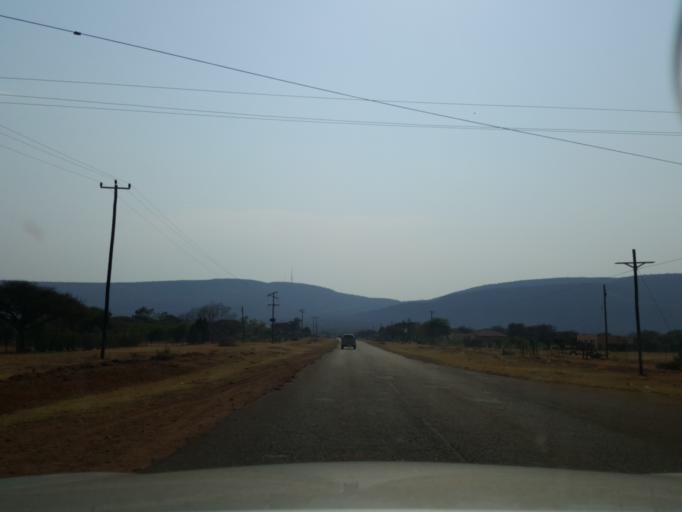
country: BW
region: South East
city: Lobatse
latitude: -25.2970
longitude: 25.8409
